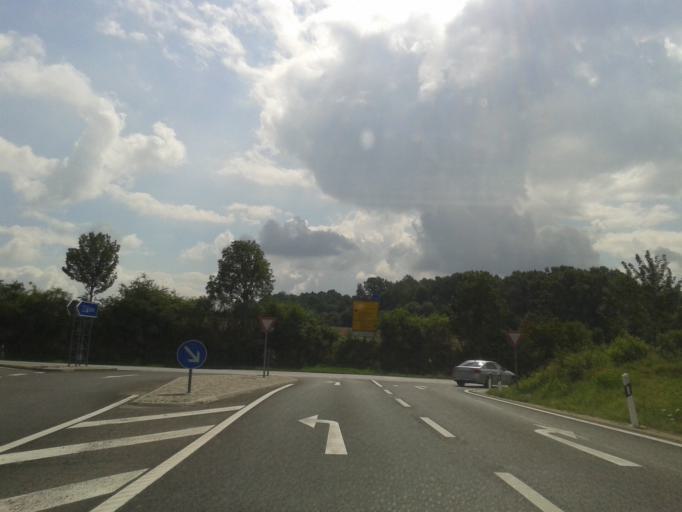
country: DE
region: Saxony
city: Goda
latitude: 51.1910
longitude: 14.3597
